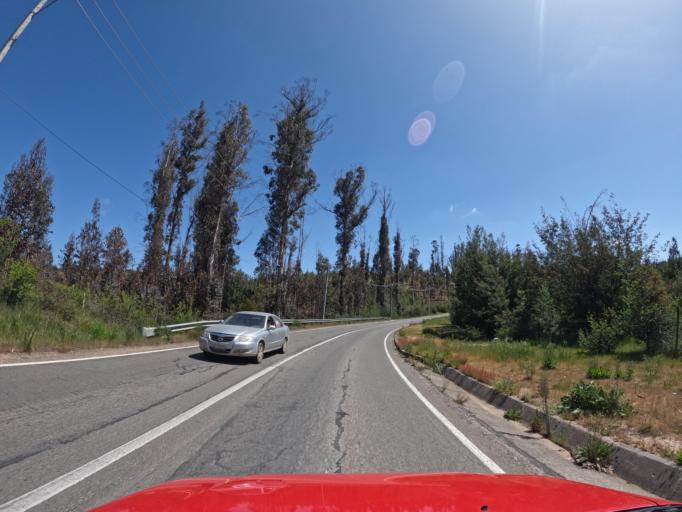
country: CL
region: O'Higgins
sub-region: Provincia de Colchagua
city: Santa Cruz
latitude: -34.6619
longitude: -71.8526
